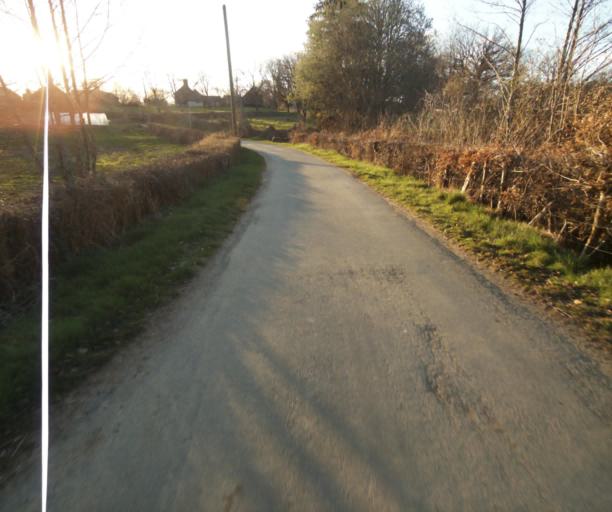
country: FR
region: Limousin
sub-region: Departement de la Correze
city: Uzerche
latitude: 45.3605
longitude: 1.5917
